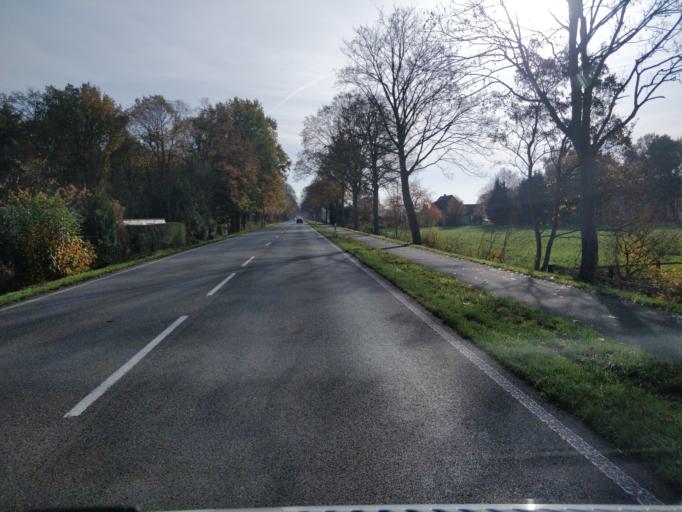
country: DE
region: North Rhine-Westphalia
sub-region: Regierungsbezirk Dusseldorf
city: Mehrhoog
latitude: 51.7341
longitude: 6.5016
